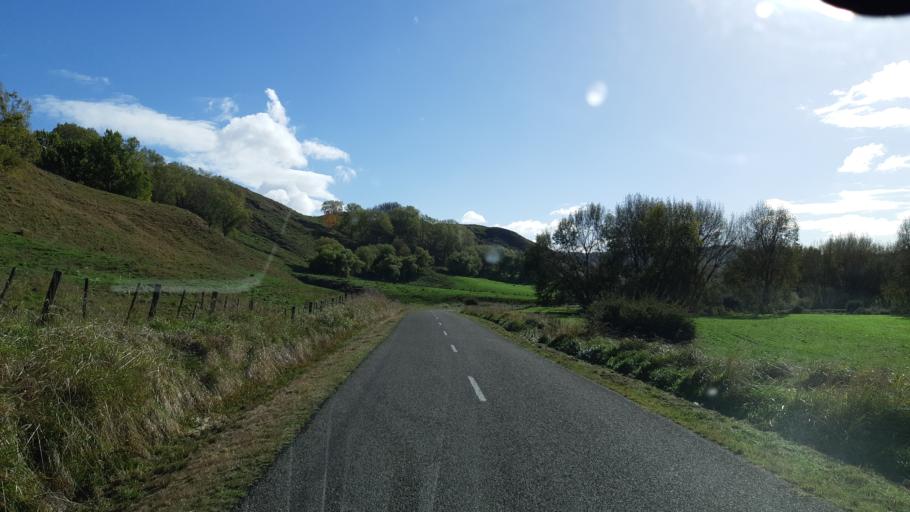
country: NZ
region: Manawatu-Wanganui
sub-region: Wanganui District
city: Wanganui
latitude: -39.8966
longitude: 175.3110
